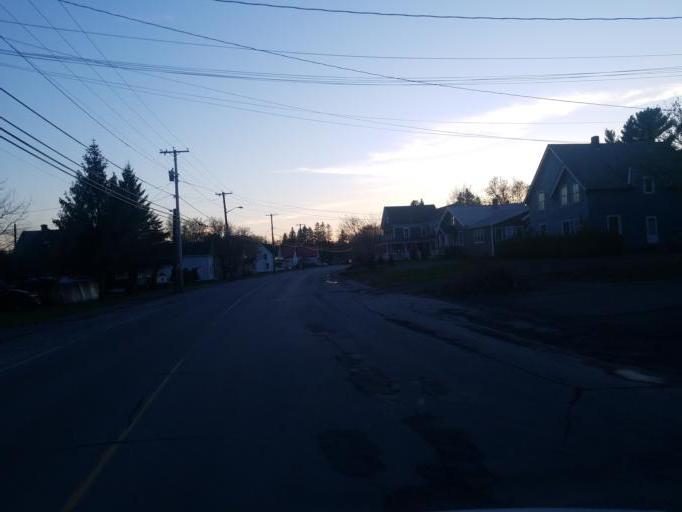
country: US
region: Maine
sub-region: Aroostook County
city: Caribou
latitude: 46.8597
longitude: -68.0210
